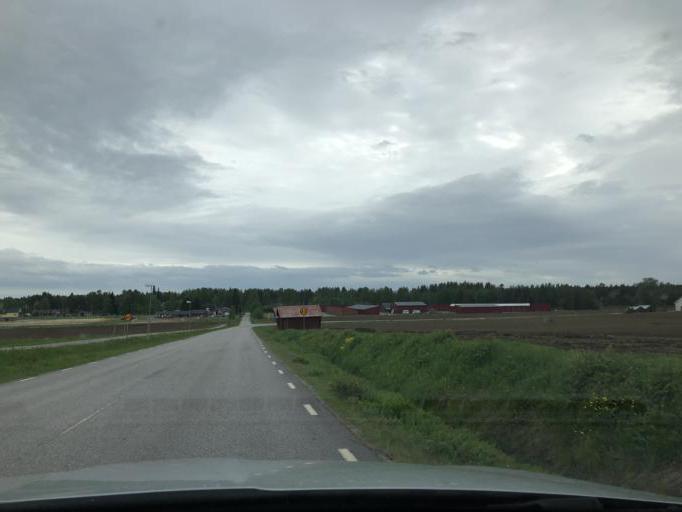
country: SE
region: Norrbotten
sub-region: Pitea Kommun
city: Bergsviken
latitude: 65.3823
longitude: 21.3136
